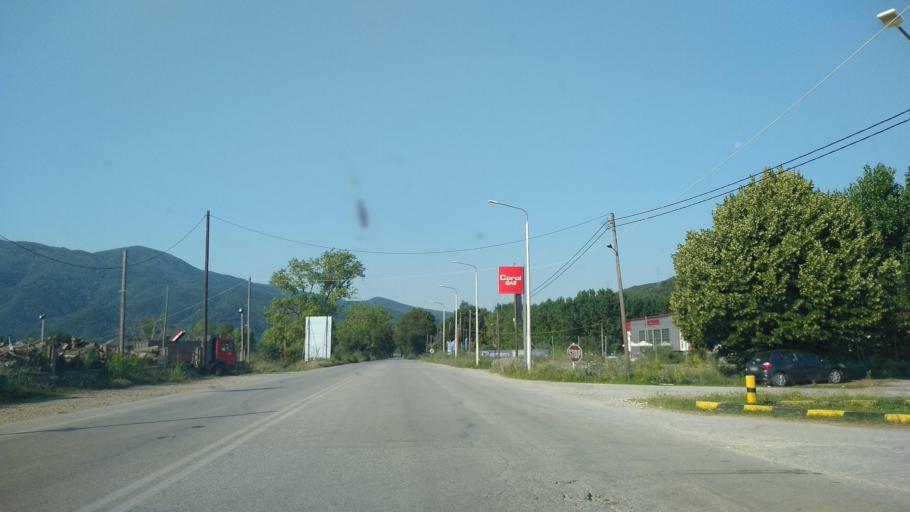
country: GR
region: Central Macedonia
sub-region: Nomos Thessalonikis
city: Nea Vrasna
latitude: 40.6876
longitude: 23.6797
